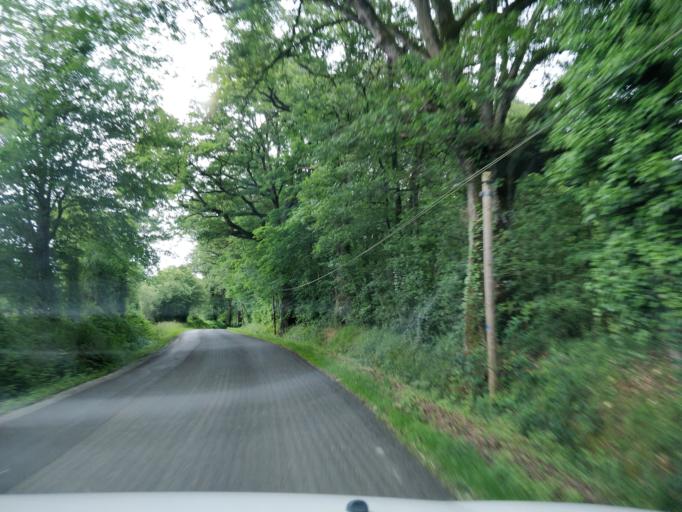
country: FR
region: Pays de la Loire
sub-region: Departement de Maine-et-Loire
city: Feneu
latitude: 47.5967
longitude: -0.6107
